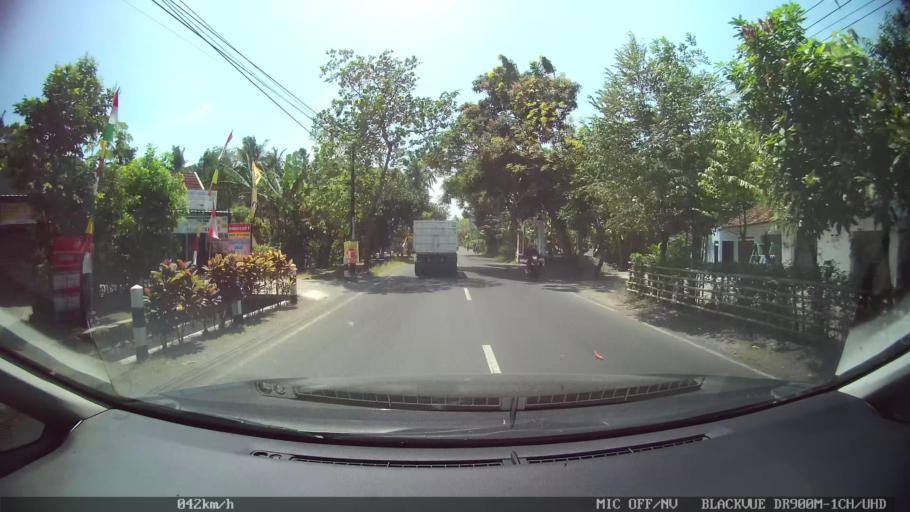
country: ID
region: Daerah Istimewa Yogyakarta
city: Srandakan
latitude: -7.9453
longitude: 110.2266
